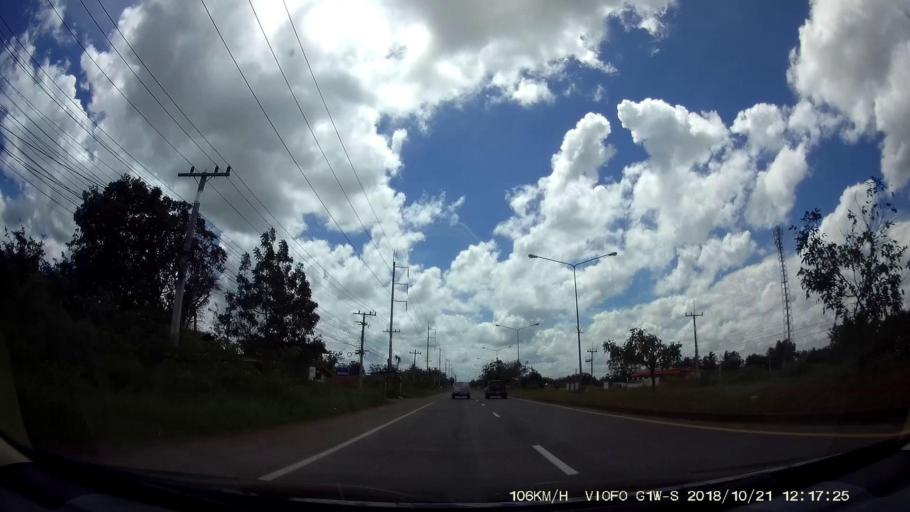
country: TH
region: Nakhon Ratchasima
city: Dan Khun Thot
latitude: 15.3324
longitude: 101.8206
